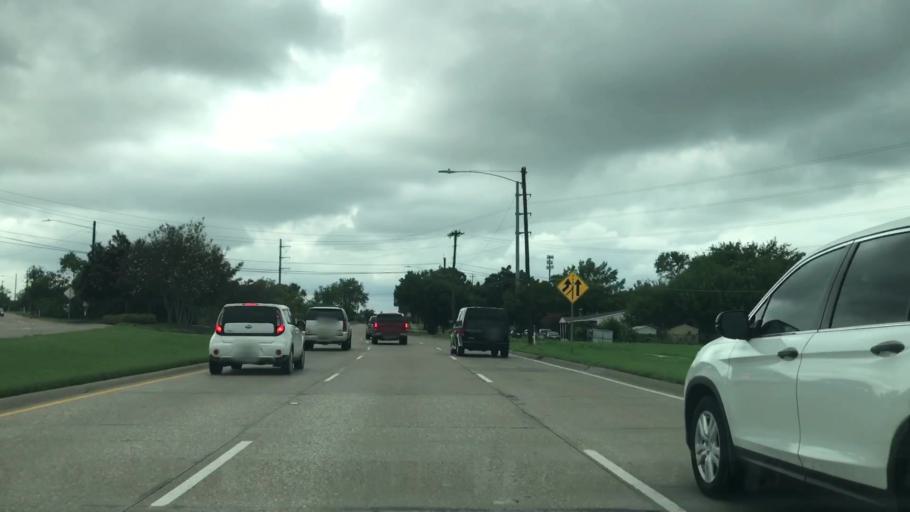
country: US
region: Texas
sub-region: Dallas County
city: Garland
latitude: 32.9088
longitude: -96.6228
